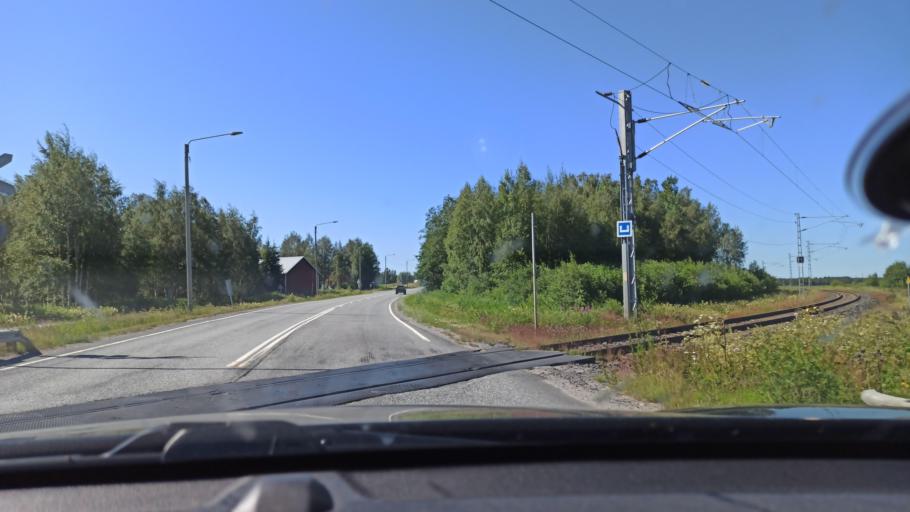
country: FI
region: Ostrobothnia
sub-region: Jakobstadsregionen
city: Bennaes
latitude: 63.6082
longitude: 22.7750
